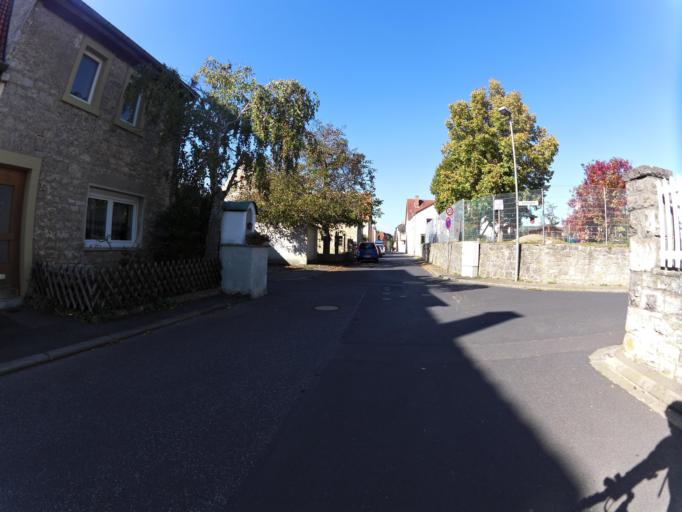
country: DE
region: Bavaria
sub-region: Regierungsbezirk Unterfranken
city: Ochsenfurt
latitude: 49.6710
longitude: 10.0521
